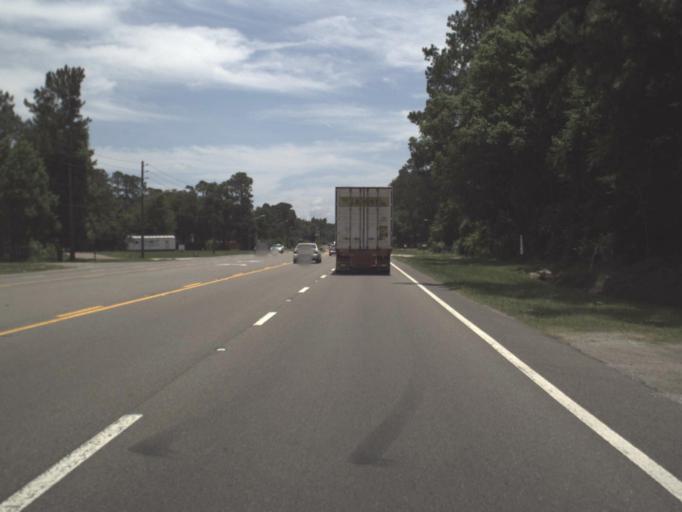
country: US
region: Florida
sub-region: Duval County
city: Jacksonville
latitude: 30.4023
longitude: -81.7420
